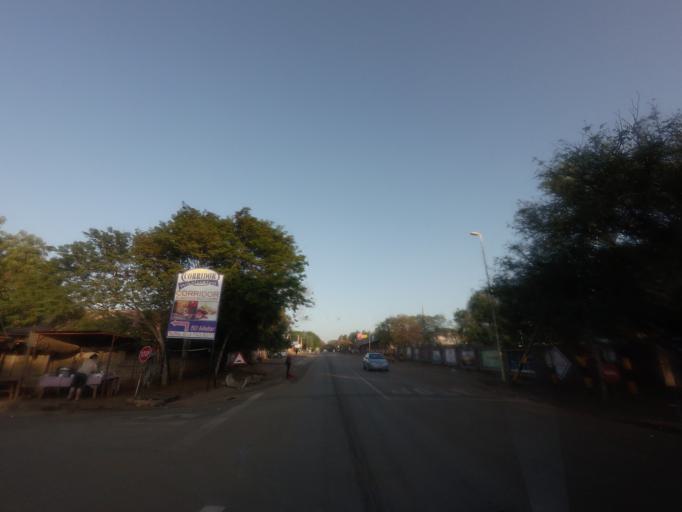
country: ZA
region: Mpumalanga
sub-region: Ehlanzeni District
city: Komatipoort
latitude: -25.4349
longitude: 31.9555
